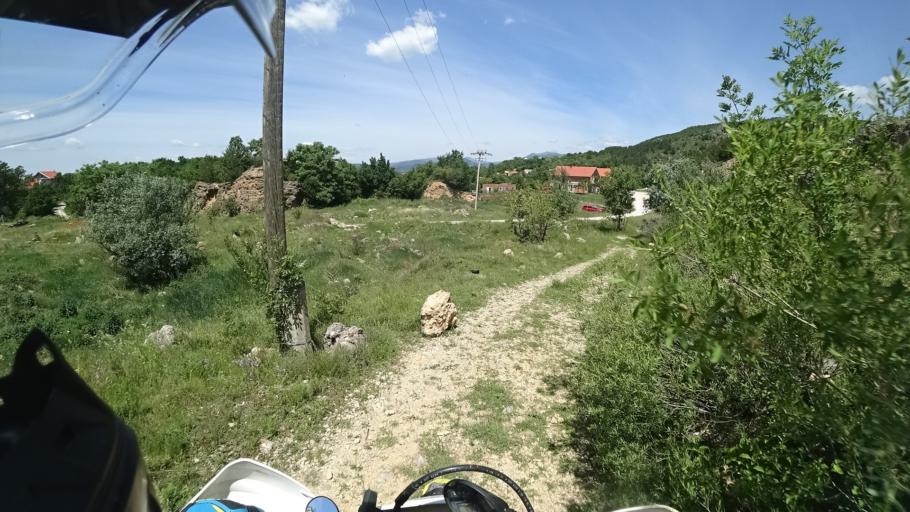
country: HR
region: Sibensko-Kniniska
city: Knin
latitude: 44.0375
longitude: 16.2304
